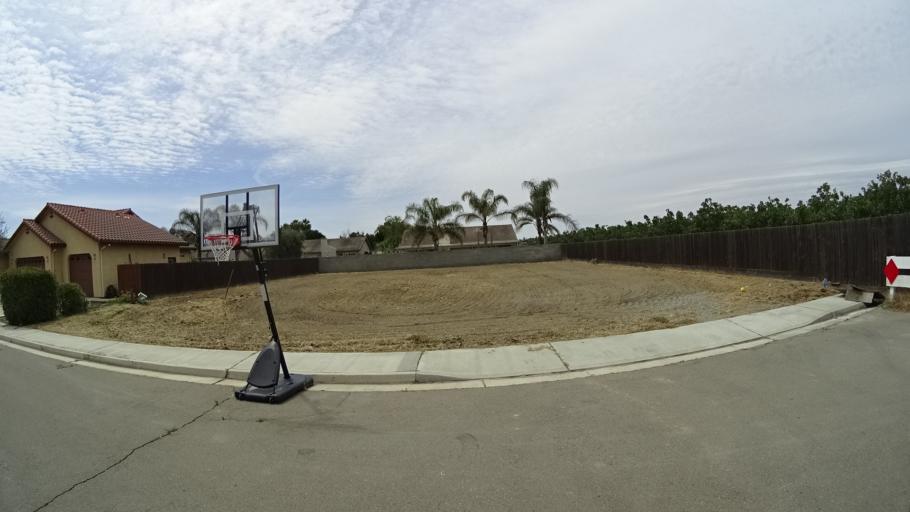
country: US
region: California
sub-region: Kings County
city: Lucerne
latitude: 36.3693
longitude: -119.6403
